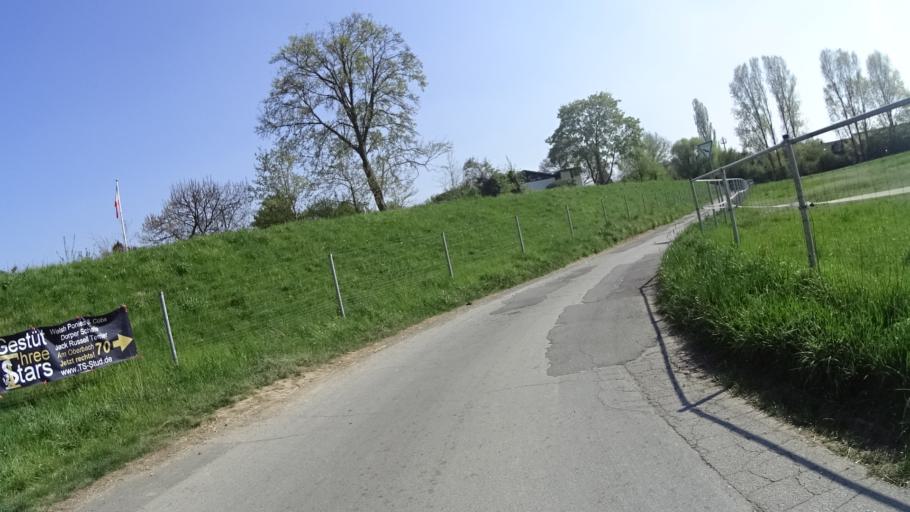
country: DE
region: North Rhine-Westphalia
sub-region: Regierungsbezirk Dusseldorf
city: Meerbusch
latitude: 51.2927
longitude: 6.7094
